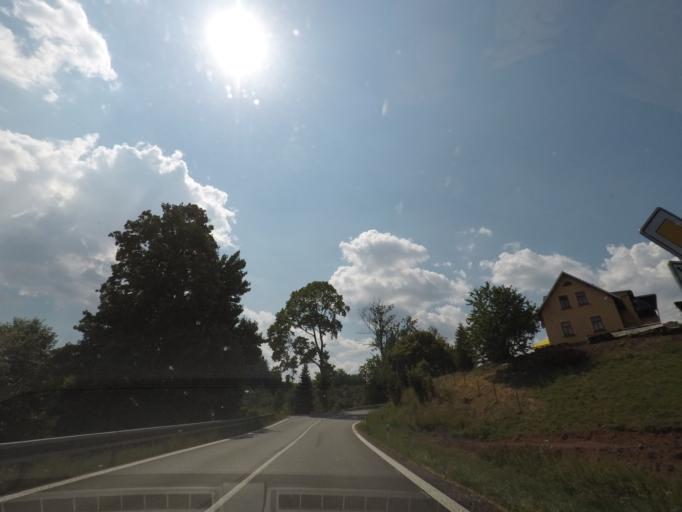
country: CZ
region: Kralovehradecky
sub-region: Okres Trutnov
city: Hostinne
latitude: 50.5171
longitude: 15.7550
